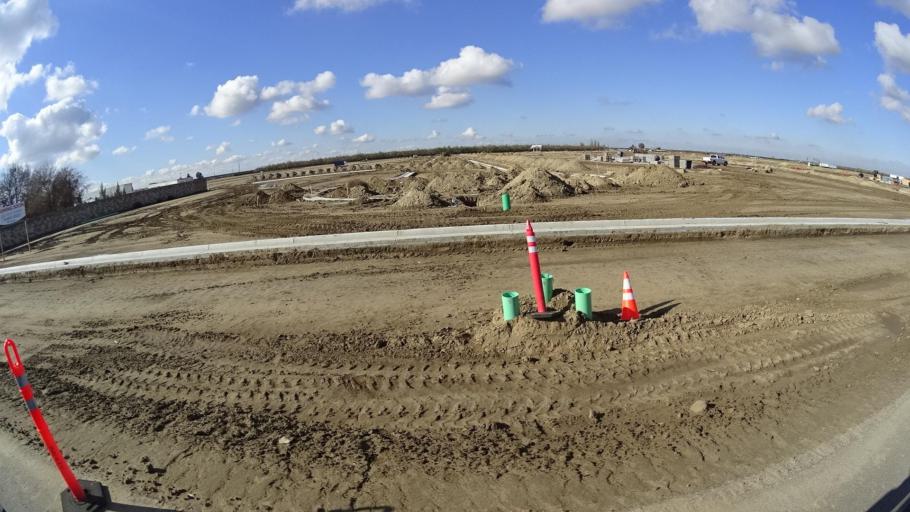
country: US
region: California
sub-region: Kern County
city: McFarland
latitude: 35.6656
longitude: -119.2410
